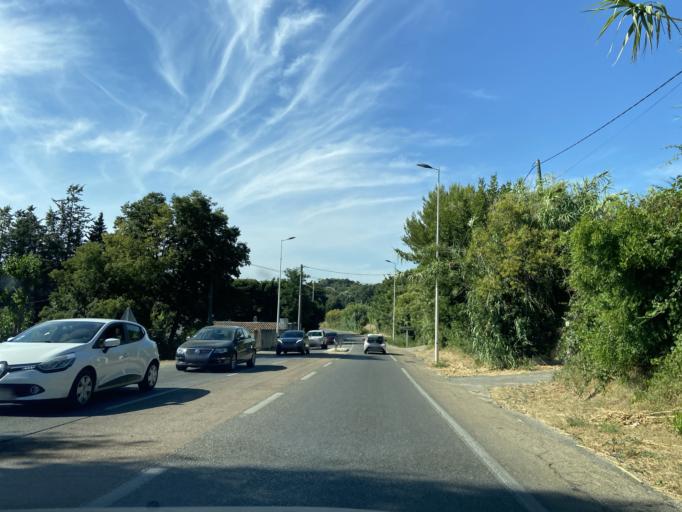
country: FR
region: Provence-Alpes-Cote d'Azur
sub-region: Departement des Bouches-du-Rhone
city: Saint-Chamas
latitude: 43.5577
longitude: 5.0320
